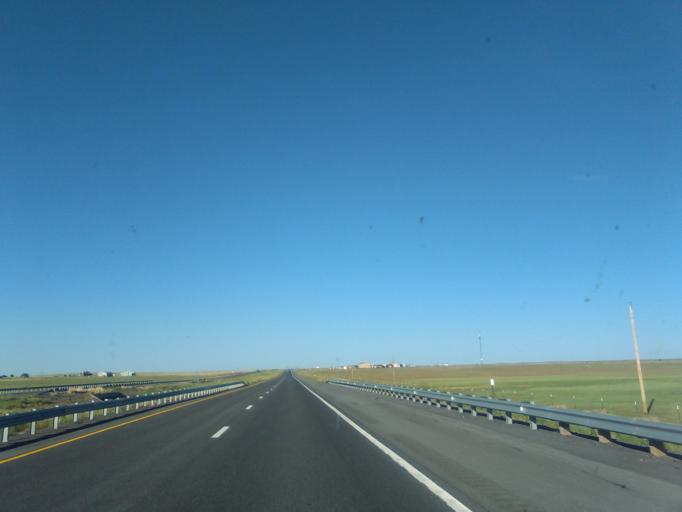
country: US
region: New Mexico
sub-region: San Miguel County
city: Las Vegas
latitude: 35.6898
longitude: -105.1328
